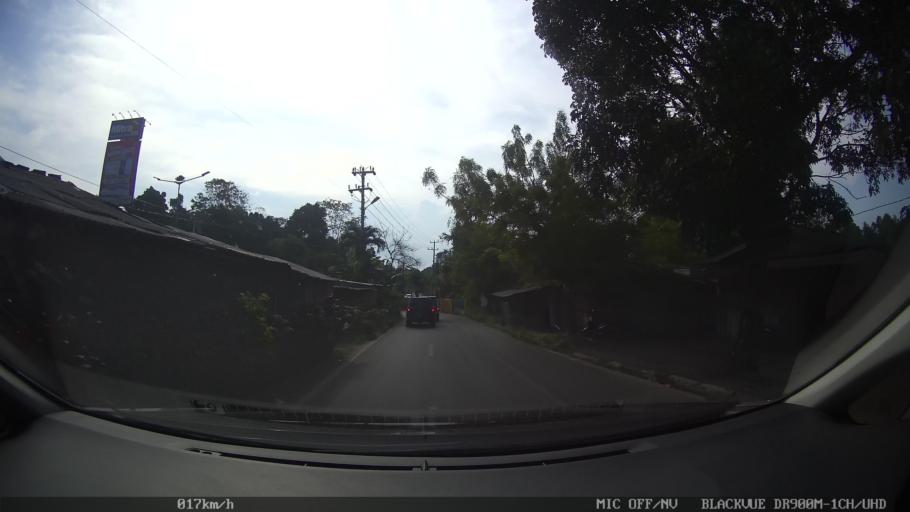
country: ID
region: Lampung
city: Kedaton
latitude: -5.3649
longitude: 105.2299
